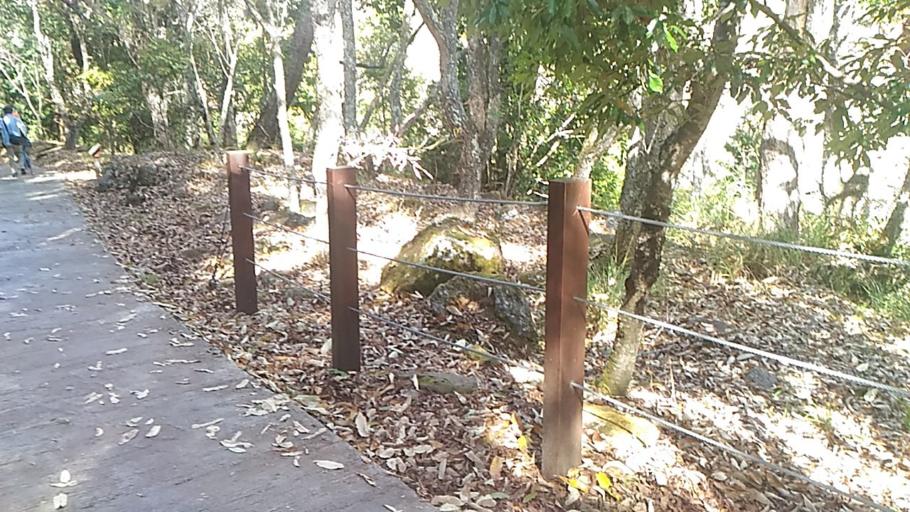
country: TW
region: Taiwan
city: Daxi
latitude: 24.3971
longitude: 121.3081
